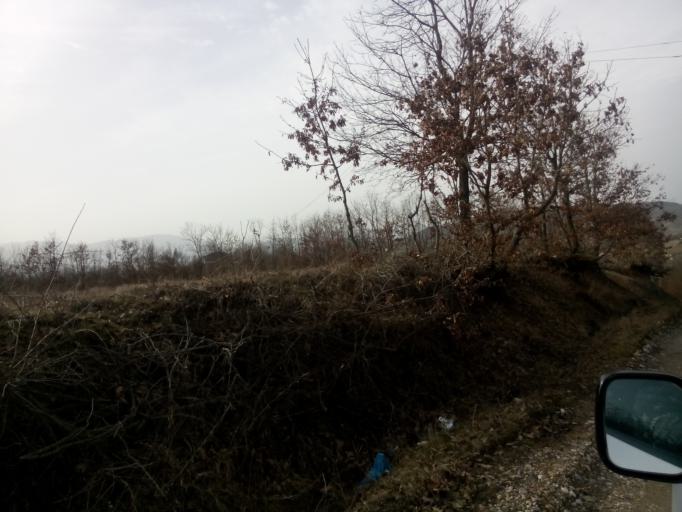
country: AL
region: Diber
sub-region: Rrethi i Matit
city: Rukaj
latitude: 41.6826
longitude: 19.9984
